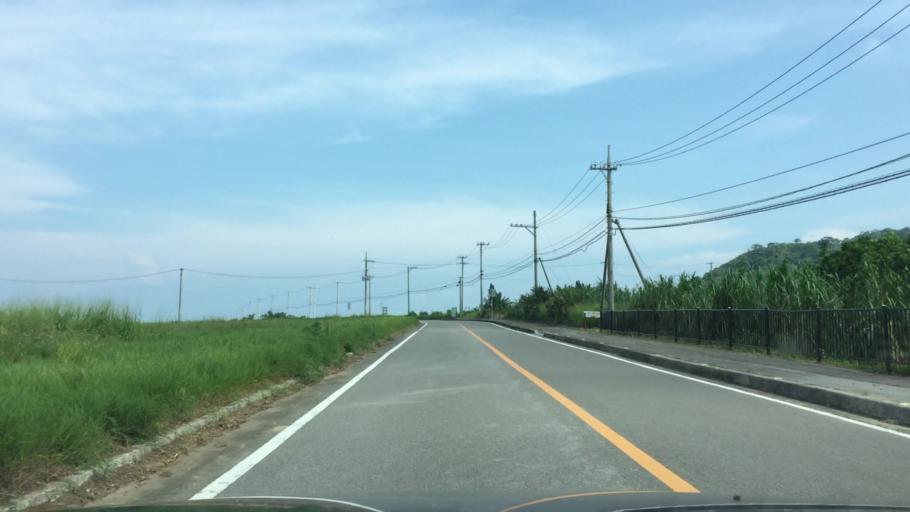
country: JP
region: Okinawa
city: Ishigaki
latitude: 24.5075
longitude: 124.2704
